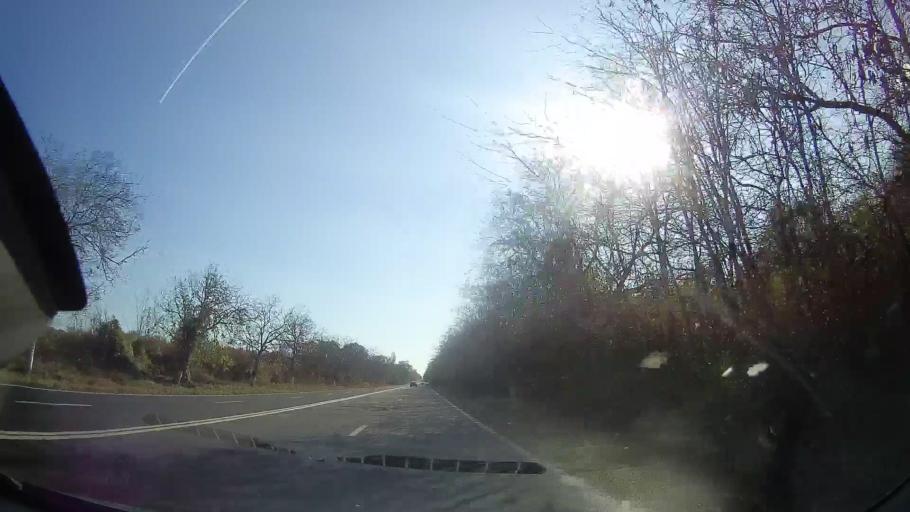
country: RO
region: Constanta
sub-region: Comuna Douazeci si Trei August
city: Dulcesti
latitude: 43.8795
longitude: 28.5736
